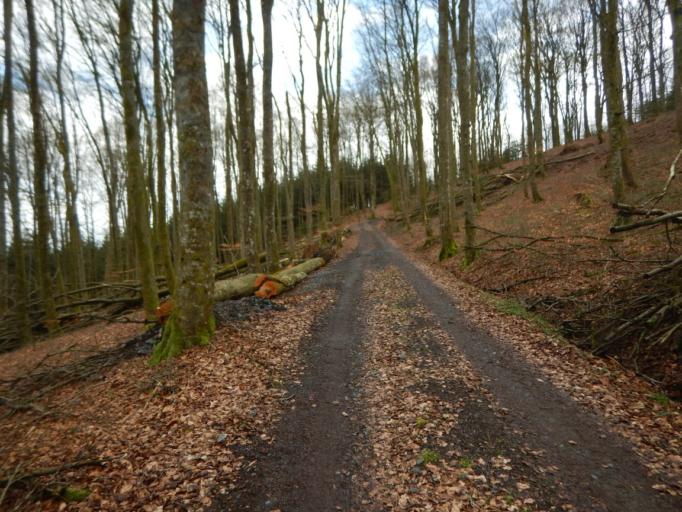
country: LU
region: Diekirch
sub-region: Canton de Wiltz
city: Esch-sur-Sure
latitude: 49.9296
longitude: 5.9087
